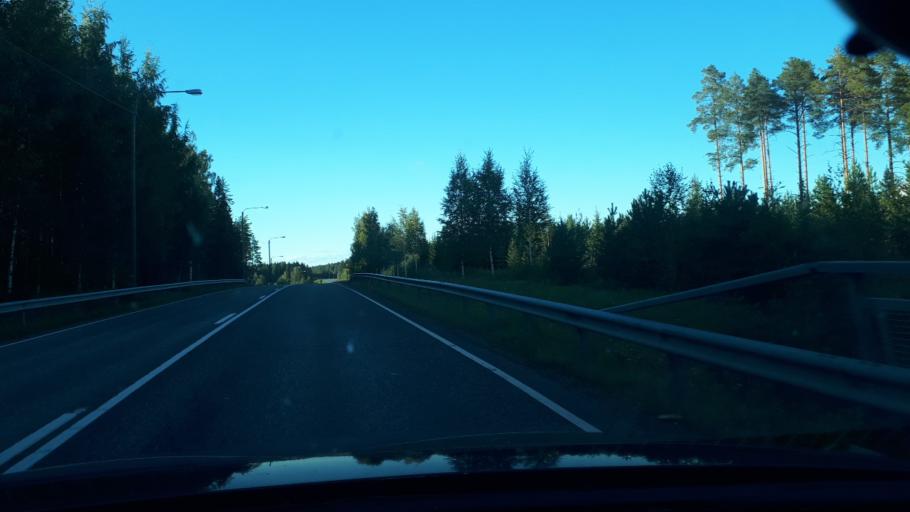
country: FI
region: Northern Savo
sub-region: Ylae-Savo
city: Lapinlahti
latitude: 63.4309
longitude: 27.3278
